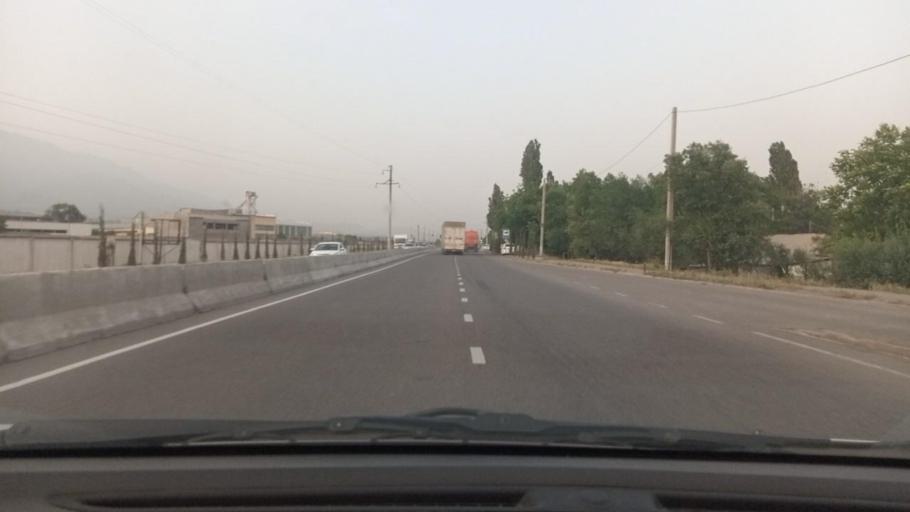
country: UZ
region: Toshkent
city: Angren
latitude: 41.0211
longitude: 70.1227
